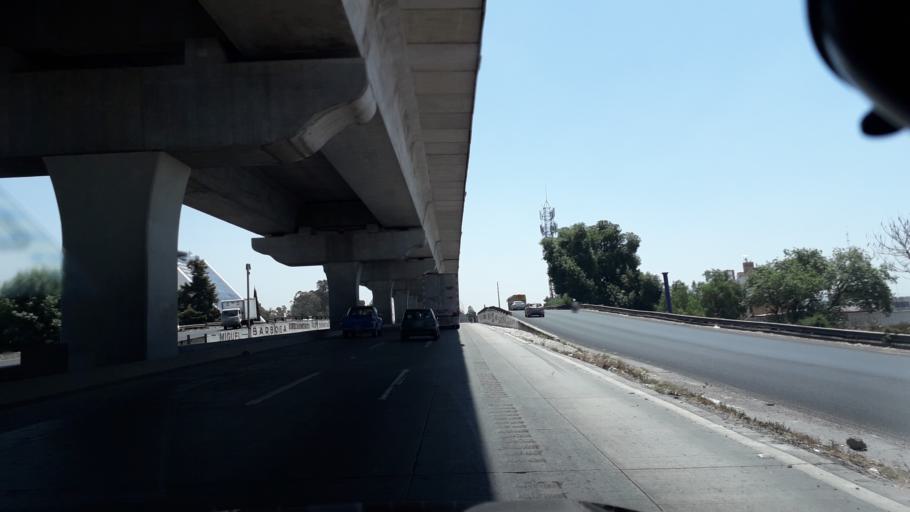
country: MX
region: Puebla
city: Puebla
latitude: 19.0863
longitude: -98.2013
